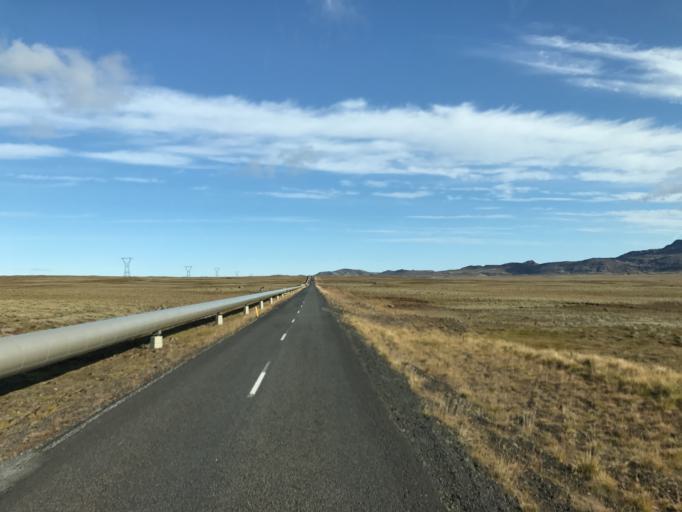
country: IS
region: Capital Region
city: Mosfellsbaer
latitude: 64.1183
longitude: -21.4429
